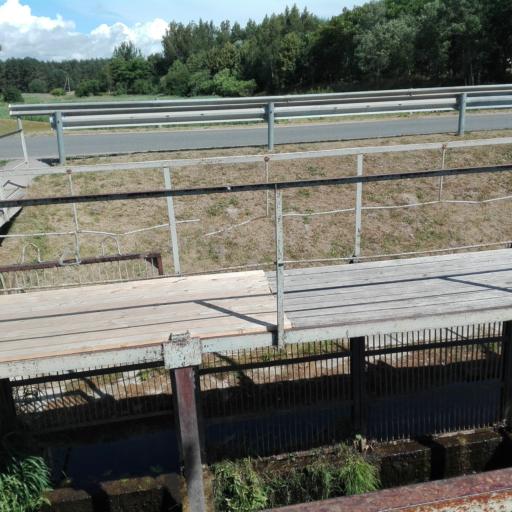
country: LT
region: Panevezys
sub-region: Birzai
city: Birzai
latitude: 56.1842
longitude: 24.7673
